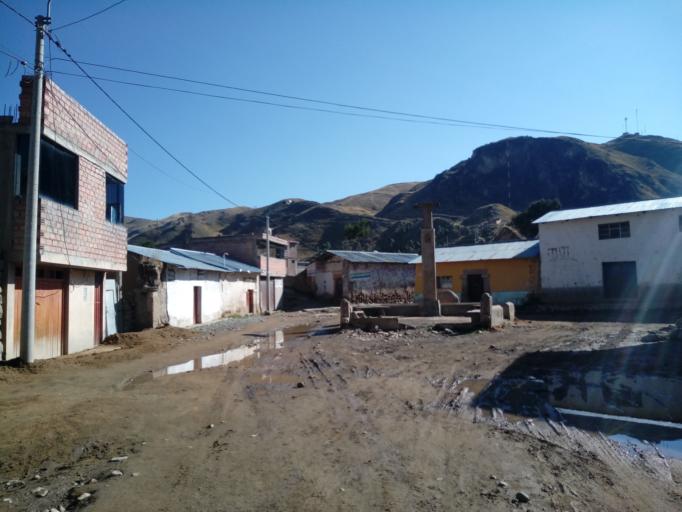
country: PE
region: Cusco
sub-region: Provincia de Chumbivilcas
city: Velille
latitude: -14.5093
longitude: -71.8858
